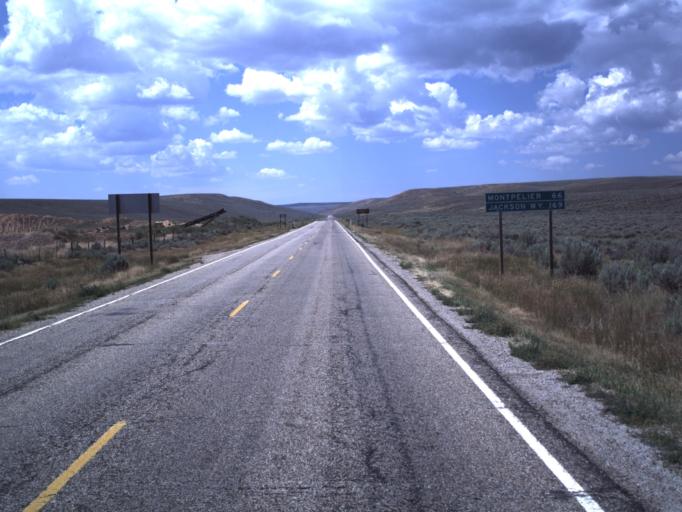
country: US
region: Utah
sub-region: Rich County
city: Randolph
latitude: 41.7719
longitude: -111.1295
